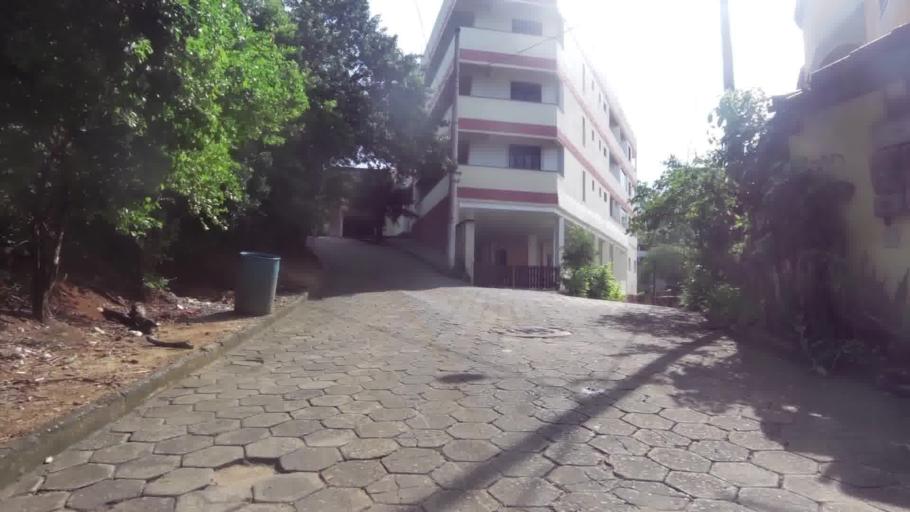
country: BR
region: Espirito Santo
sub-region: Piuma
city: Piuma
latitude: -20.8269
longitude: -40.6924
